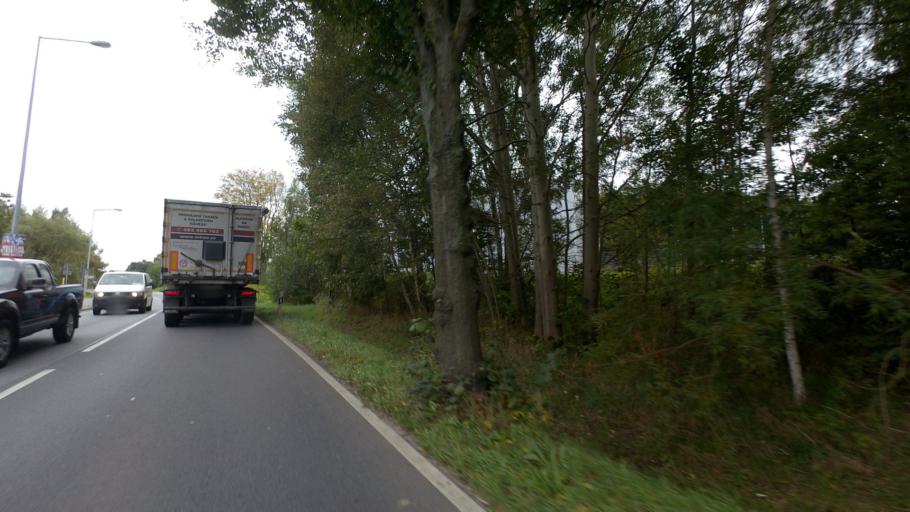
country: DE
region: Saxony
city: Bautzen
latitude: 51.1926
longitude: 14.4108
